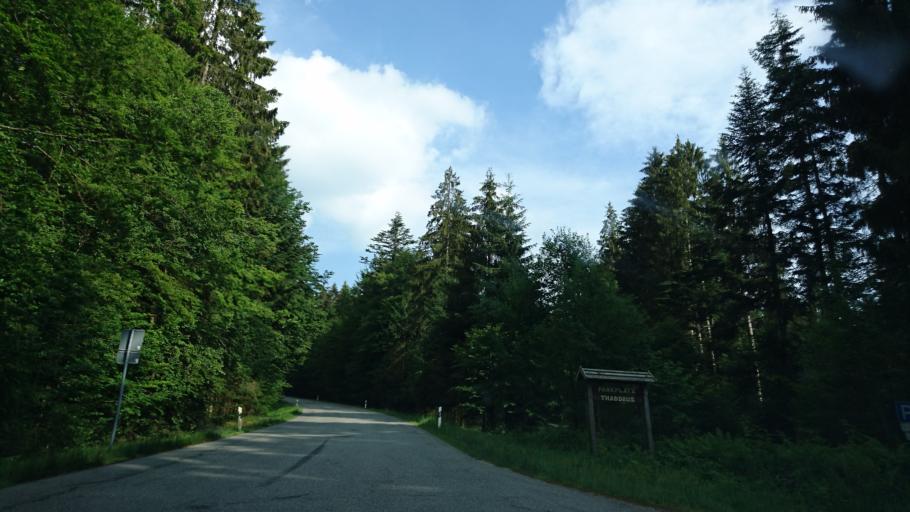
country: DE
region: Bavaria
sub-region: Lower Bavaria
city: Neuschonau
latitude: 48.8948
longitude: 13.4775
